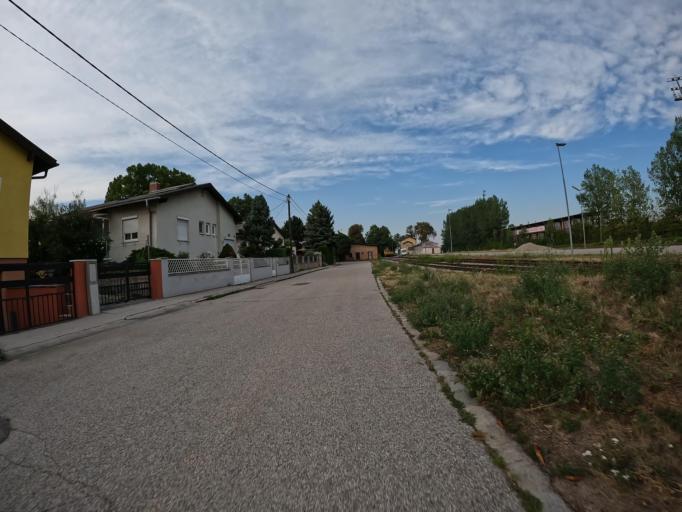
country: AT
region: Lower Austria
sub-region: Politischer Bezirk Baden
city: Traiskirchen
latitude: 48.0167
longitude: 16.3018
